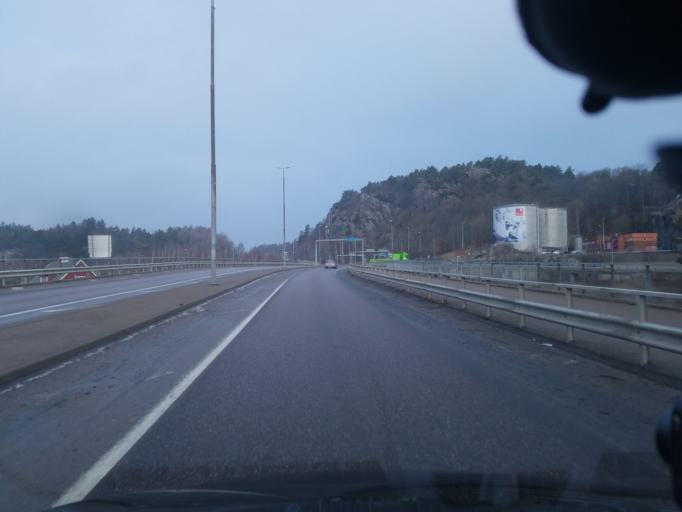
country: SE
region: Vaestra Goetaland
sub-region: Uddevalla Kommun
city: Uddevalla
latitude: 58.3546
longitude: 11.9132
